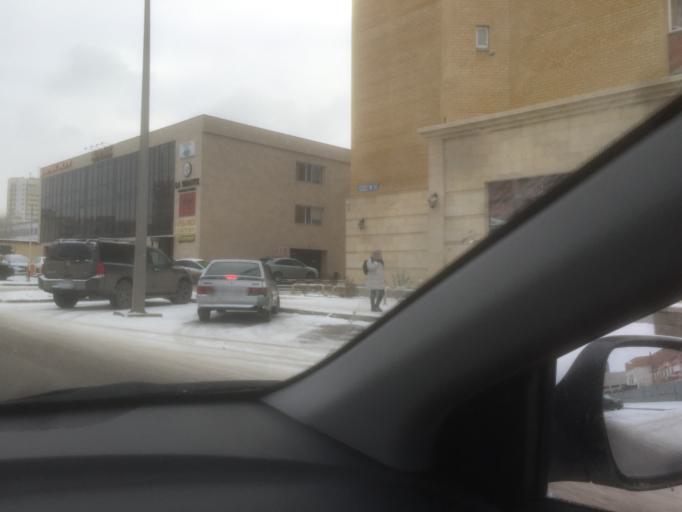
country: KZ
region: Astana Qalasy
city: Astana
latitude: 51.1433
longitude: 71.4687
